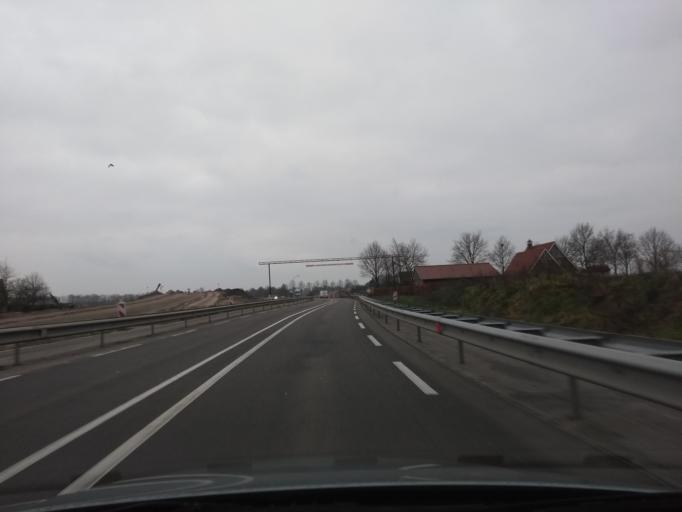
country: NL
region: Overijssel
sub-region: Gemeente Haaksbergen
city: Haaksbergen
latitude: 52.1845
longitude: 6.7377
